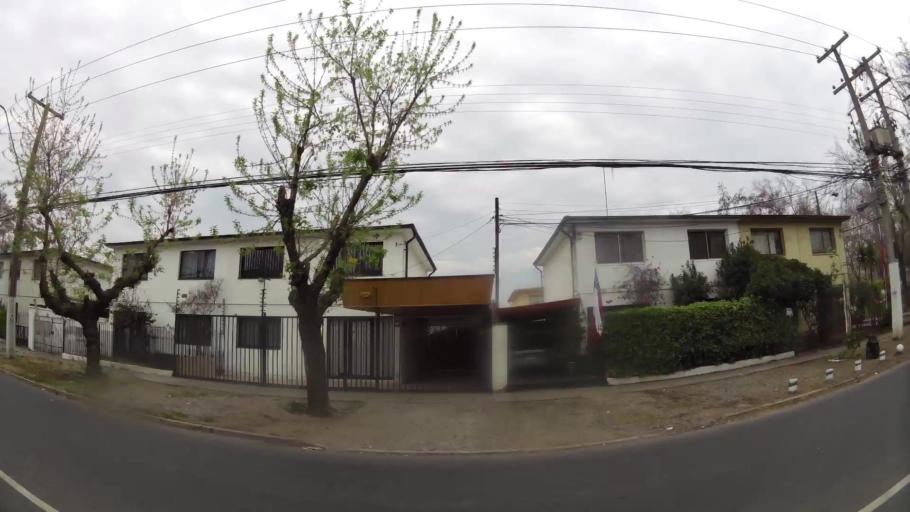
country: CL
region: Santiago Metropolitan
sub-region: Provincia de Santiago
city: Villa Presidente Frei, Nunoa, Santiago, Chile
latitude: -33.4862
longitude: -70.6062
